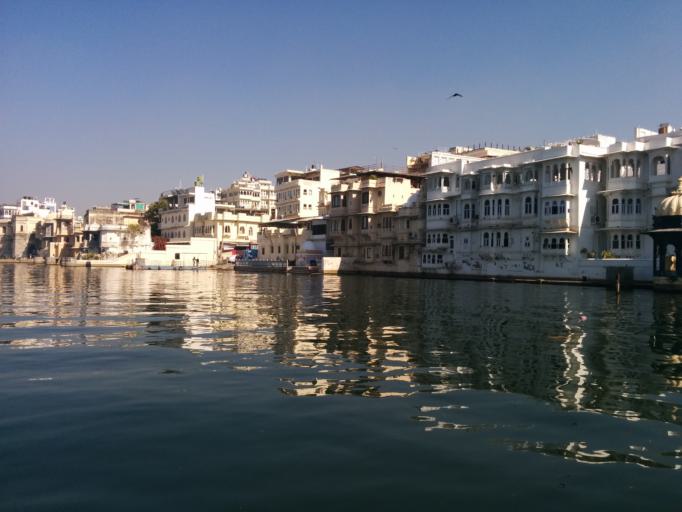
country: IN
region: Rajasthan
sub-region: Udaipur
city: Udaipur
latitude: 24.5781
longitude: 73.6819
